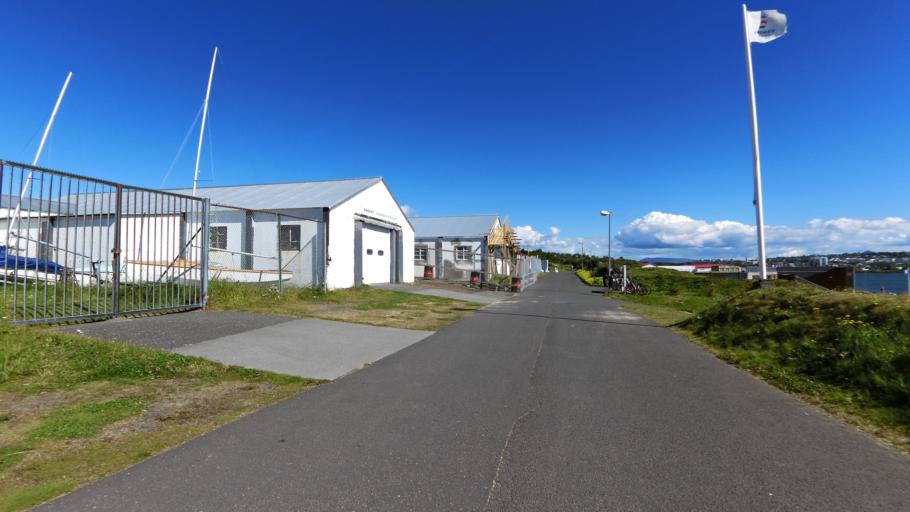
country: IS
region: Capital Region
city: Kopavogur
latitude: 64.1219
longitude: -21.9312
